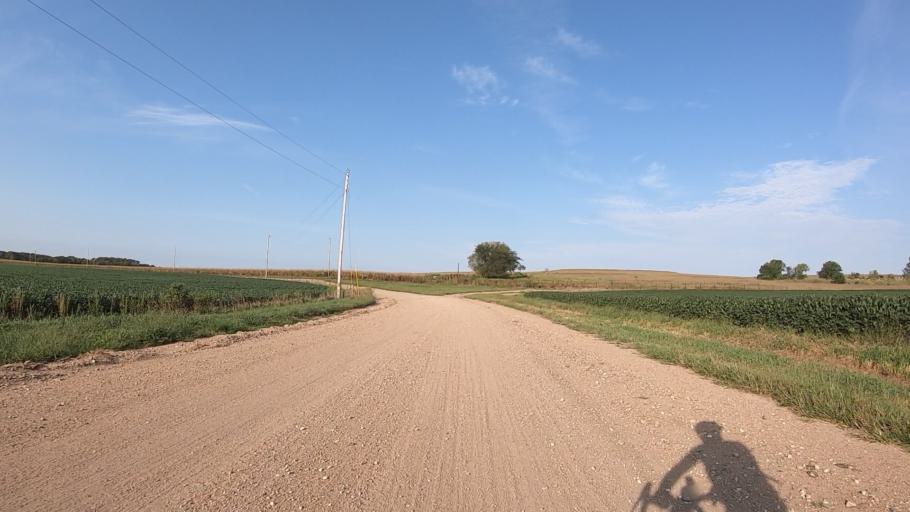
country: US
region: Kansas
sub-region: Marshall County
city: Blue Rapids
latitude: 39.6717
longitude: -96.8052
